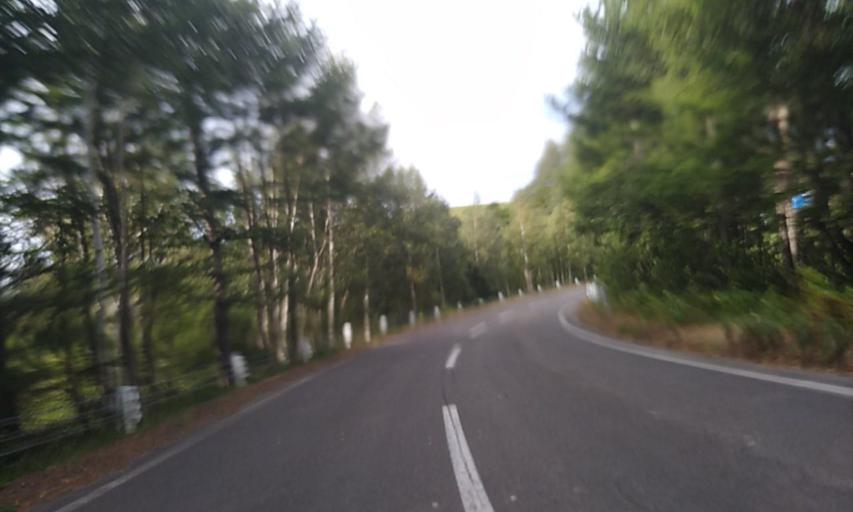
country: JP
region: Hokkaido
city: Abashiri
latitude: 43.7959
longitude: 144.5690
